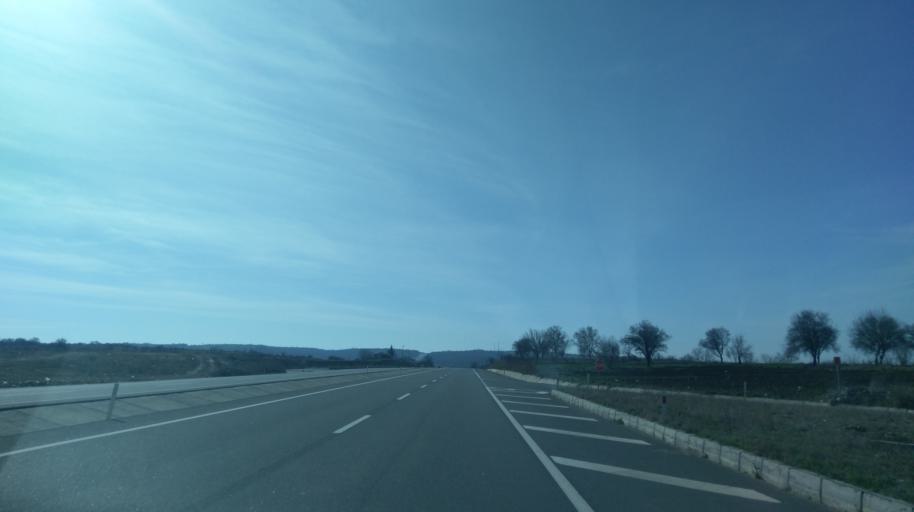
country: TR
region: Edirne
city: Ibriktepe
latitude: 40.9992
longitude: 26.6373
